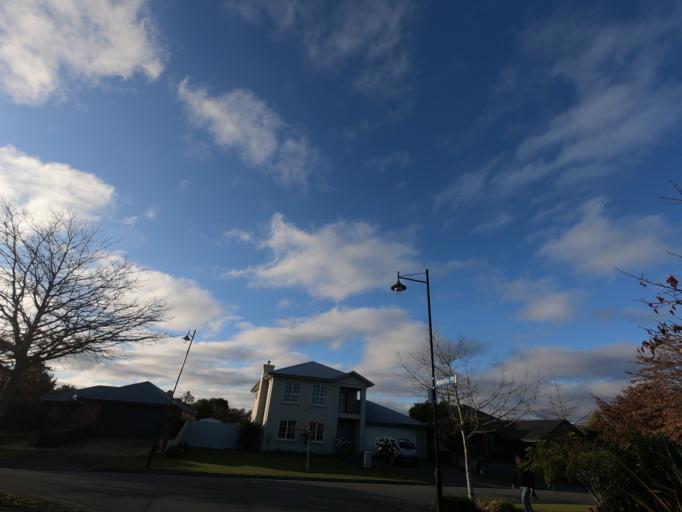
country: NZ
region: Canterbury
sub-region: Selwyn District
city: Prebbleton
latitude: -43.5665
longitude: 172.5687
